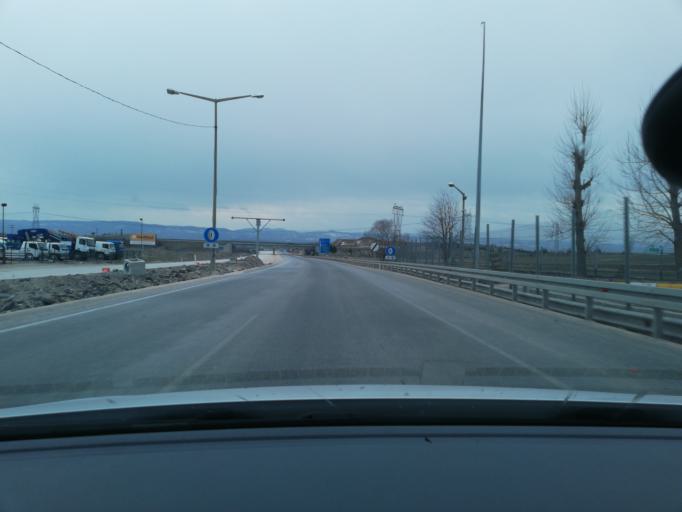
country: TR
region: Bolu
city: Gerede
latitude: 40.7837
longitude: 32.2114
